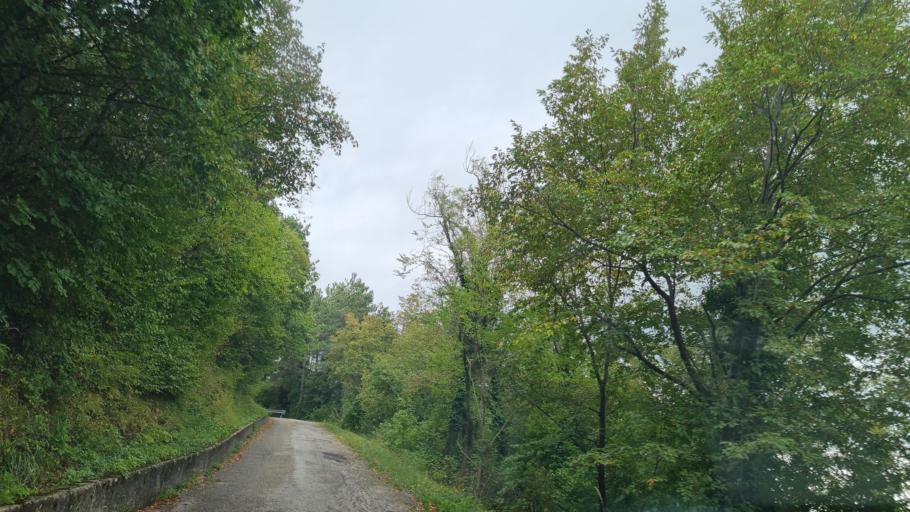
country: IT
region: Veneto
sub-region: Provincia di Vicenza
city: Marostica
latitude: 45.7888
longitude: 11.6618
